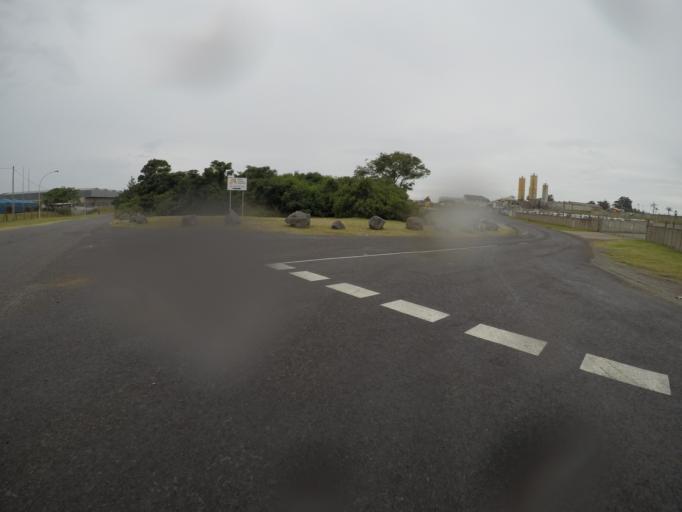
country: ZA
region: Eastern Cape
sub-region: Buffalo City Metropolitan Municipality
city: East London
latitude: -32.9749
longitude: 27.8244
